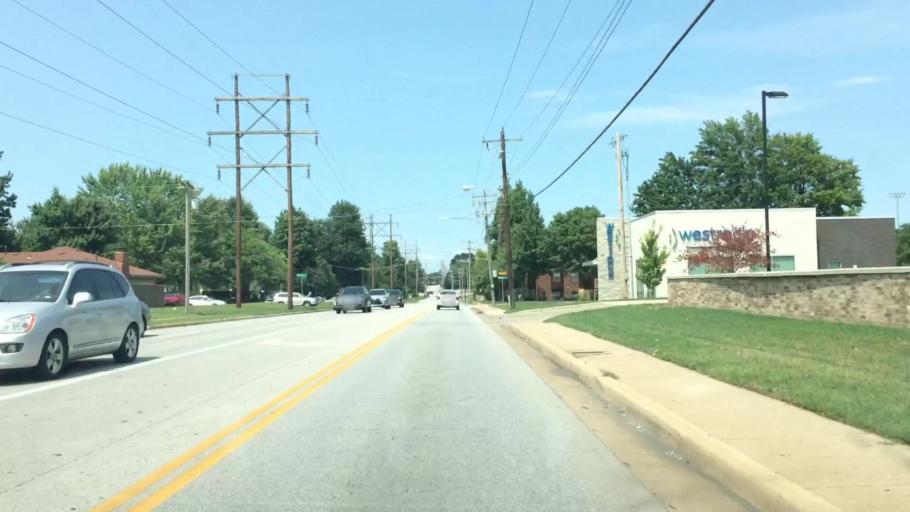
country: US
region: Missouri
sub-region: Greene County
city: Springfield
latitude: 37.1630
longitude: -93.2716
